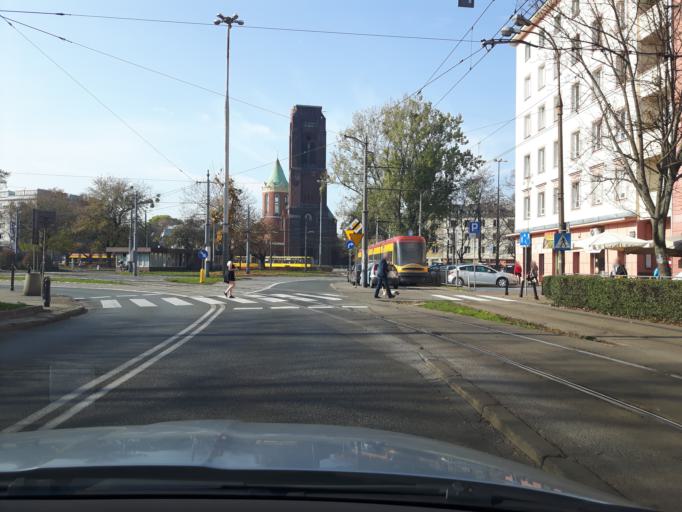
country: PL
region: Masovian Voivodeship
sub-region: Warszawa
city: Ochota
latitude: 52.2193
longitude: 20.9857
